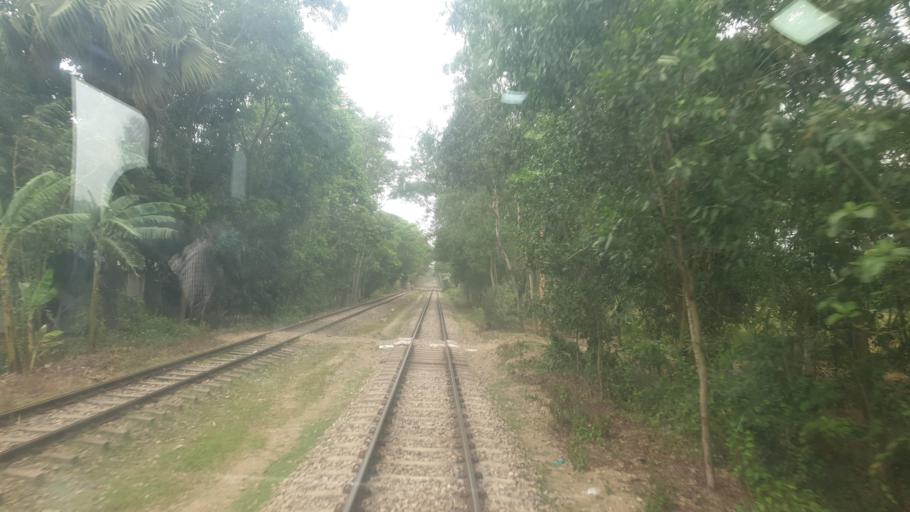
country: BD
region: Chittagong
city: Fatikchari
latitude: 22.7173
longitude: 91.6155
